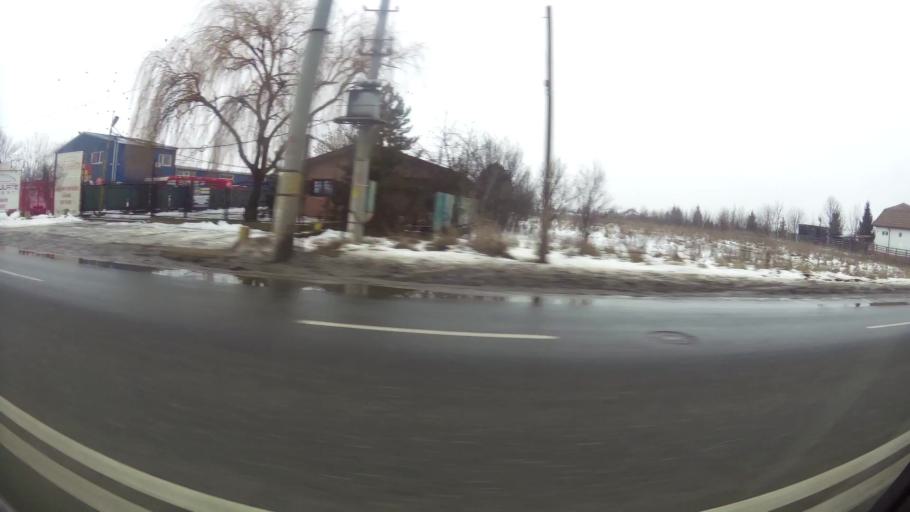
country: RO
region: Ilfov
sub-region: Comuna Magurele
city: Magurele
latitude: 44.3713
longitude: 26.0436
